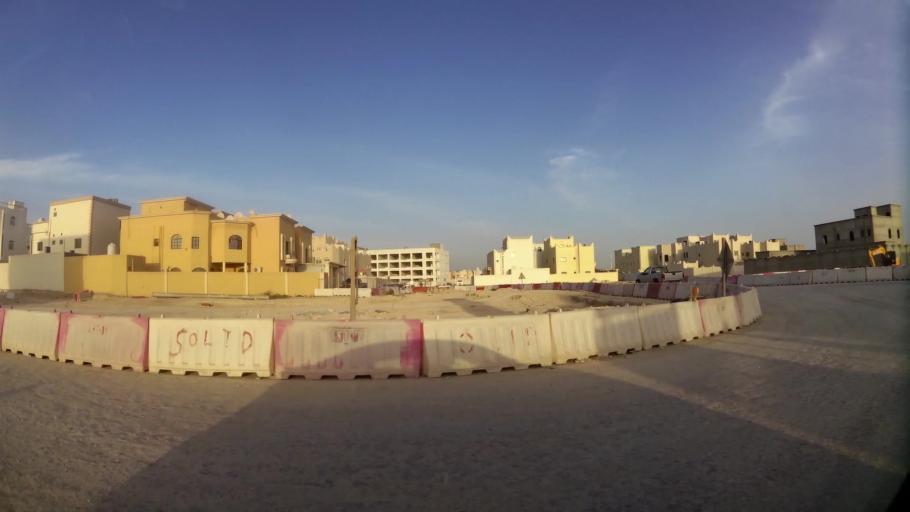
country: QA
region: Al Wakrah
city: Al Wakrah
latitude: 25.1471
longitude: 51.5950
